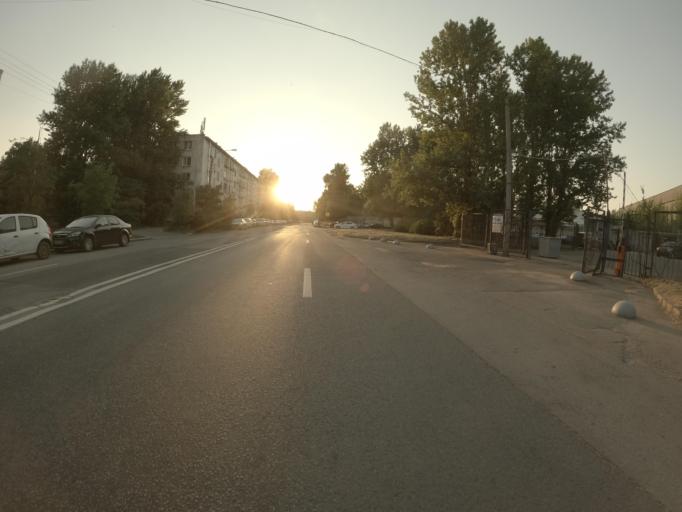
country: RU
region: St.-Petersburg
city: Avtovo
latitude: 59.8681
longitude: 30.2790
